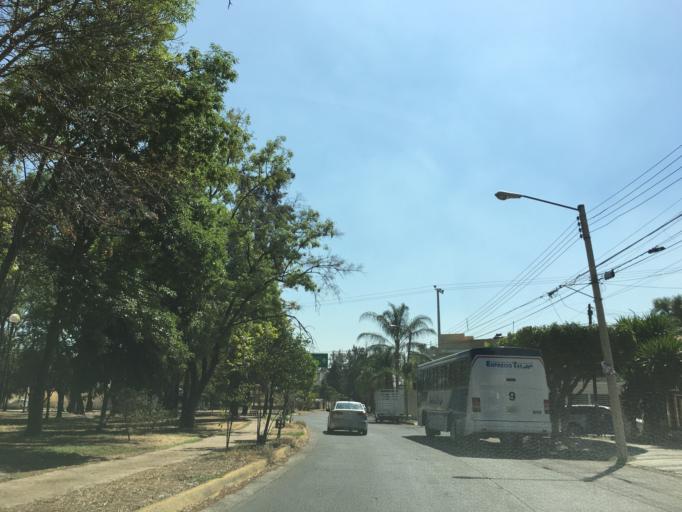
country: MX
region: Jalisco
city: Guadalajara
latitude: 20.6466
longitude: -103.3897
